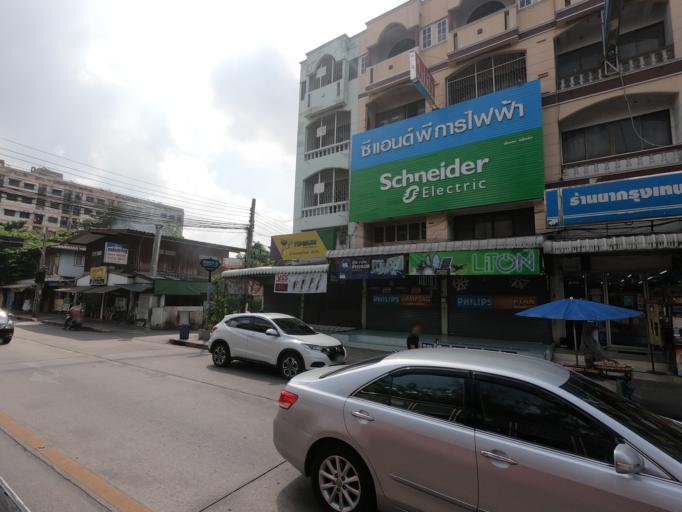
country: TH
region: Bangkok
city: Lat Phrao
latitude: 13.7953
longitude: 100.6074
